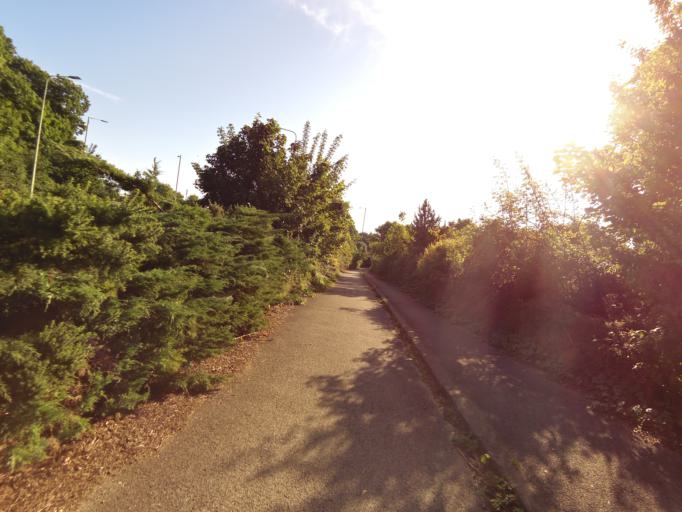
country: GB
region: England
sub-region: Suffolk
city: Kesgrave
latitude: 52.0690
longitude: 1.2685
